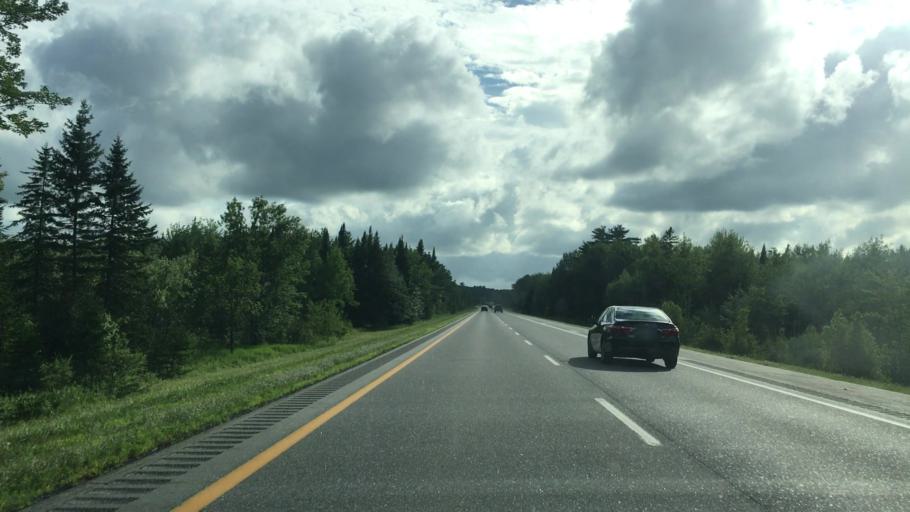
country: US
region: Maine
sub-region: Somerset County
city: Palmyra
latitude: 44.8137
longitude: -69.3462
